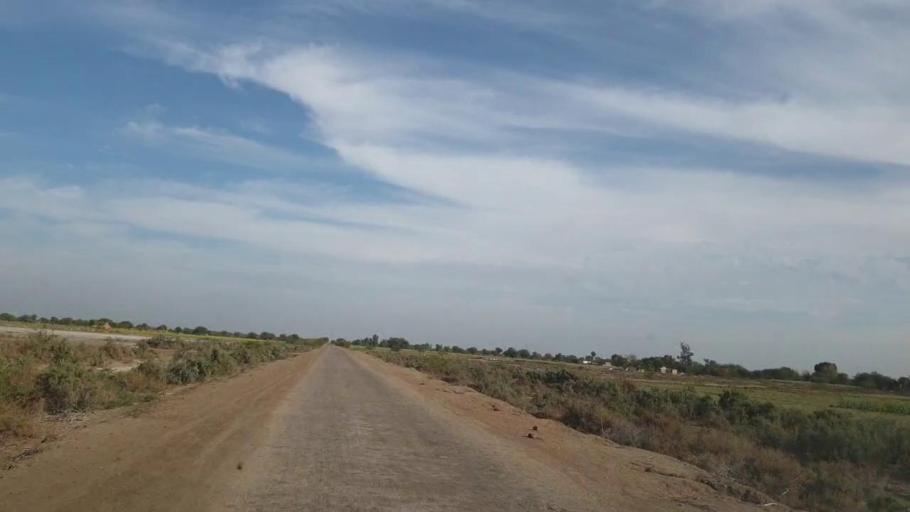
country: PK
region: Sindh
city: Pithoro
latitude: 25.6347
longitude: 69.3946
